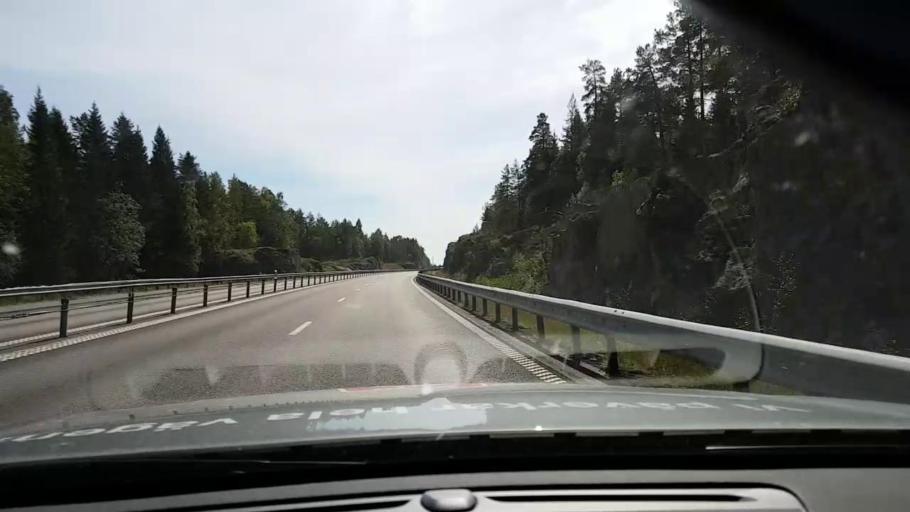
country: SE
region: Vaesternorrland
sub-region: OErnskoeldsviks Kommun
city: Husum
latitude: 63.3869
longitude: 19.1944
